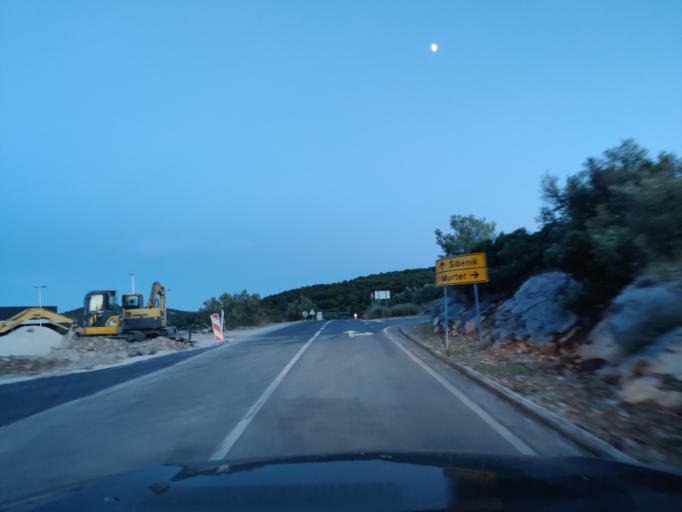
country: HR
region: Sibensko-Kniniska
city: Murter
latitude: 43.8122
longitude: 15.6018
